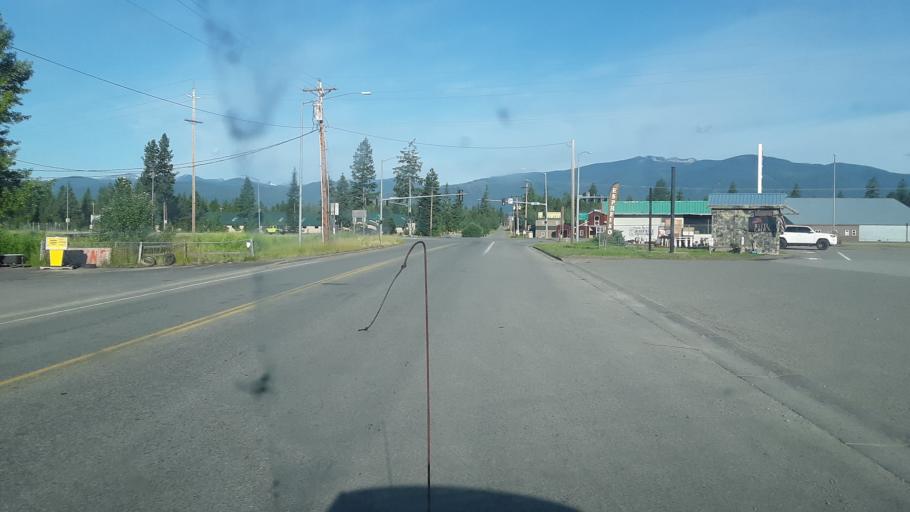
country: US
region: Idaho
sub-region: Boundary County
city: Bonners Ferry
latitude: 48.7313
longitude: -116.2983
